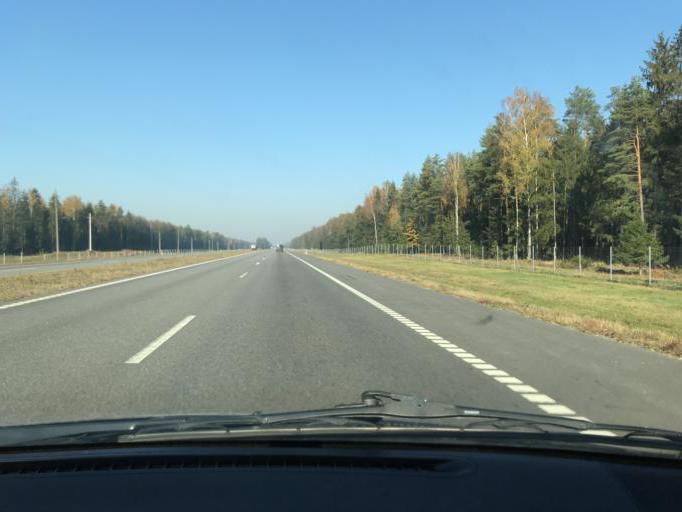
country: BY
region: Minsk
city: Slutsk
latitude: 53.2914
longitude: 27.5477
